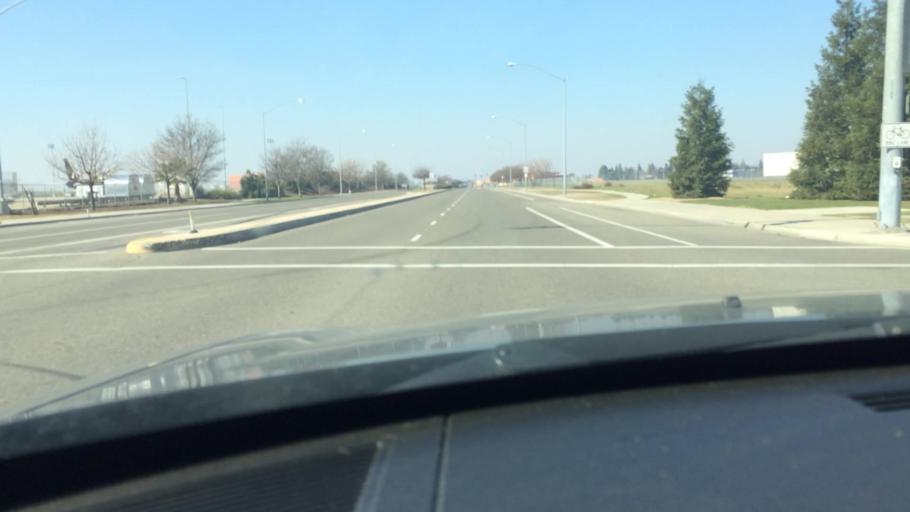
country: US
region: California
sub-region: Fresno County
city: Tarpey Village
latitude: 36.7805
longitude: -119.7104
